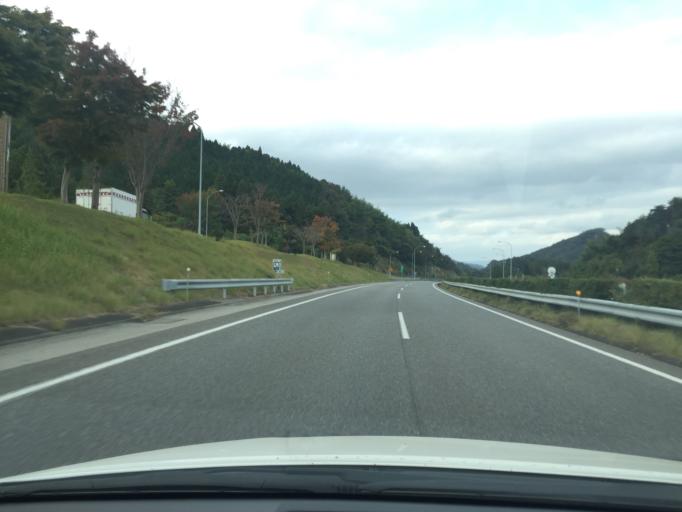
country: JP
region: Fukushima
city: Iwaki
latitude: 37.0196
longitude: 140.8131
